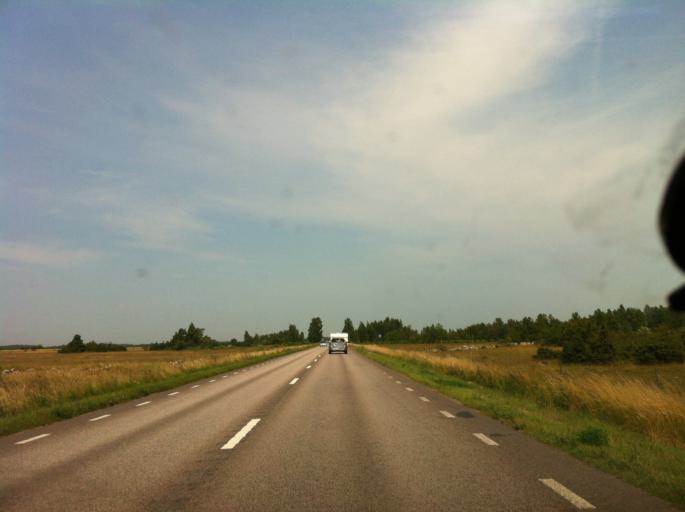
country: SE
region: Kalmar
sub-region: Borgholms Kommun
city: Borgholm
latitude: 56.9277
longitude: 16.7650
